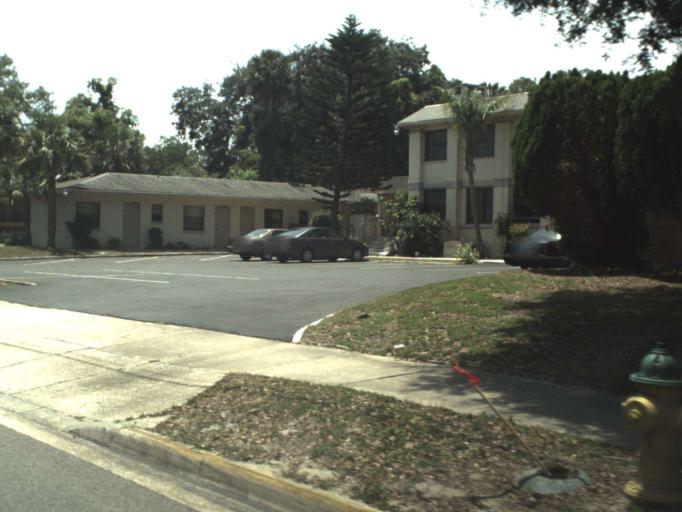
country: US
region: Florida
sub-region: Volusia County
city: Daytona Beach
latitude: 29.2024
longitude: -81.0184
